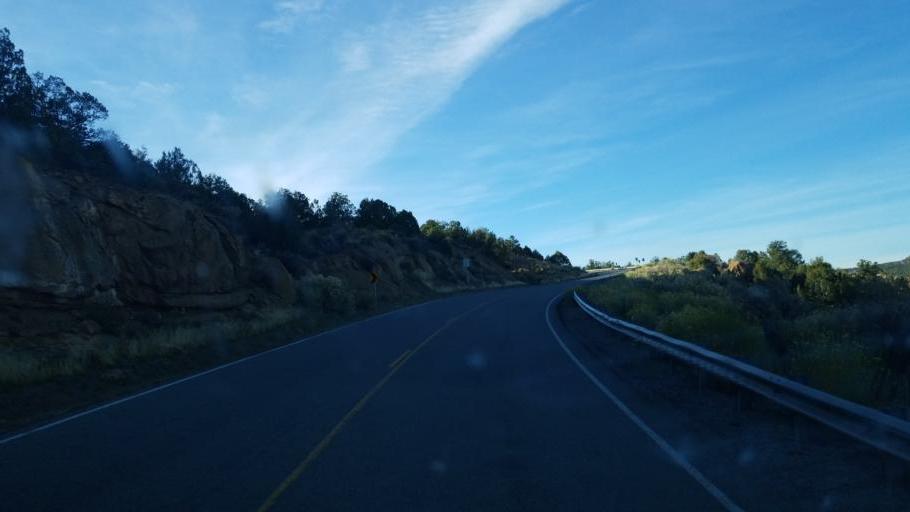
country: US
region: New Mexico
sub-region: Rio Arriba County
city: Navajo
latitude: 36.7089
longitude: -107.3182
